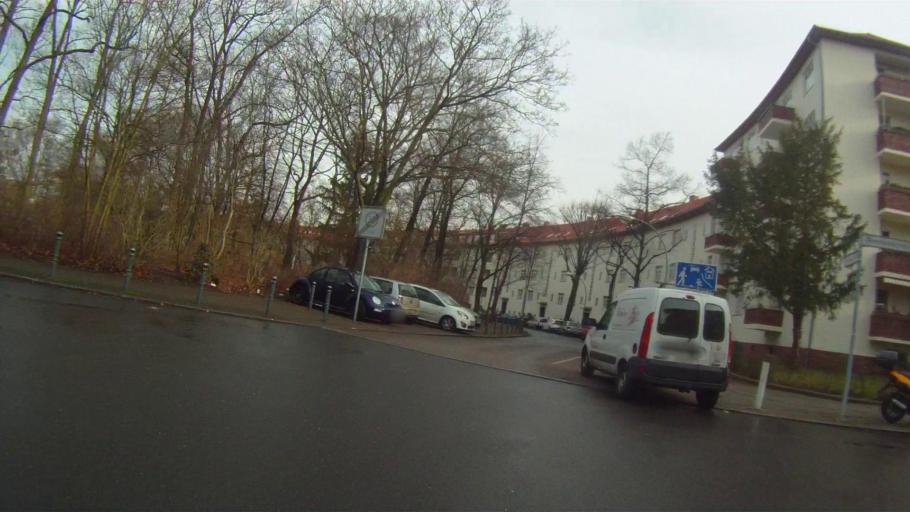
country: DE
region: Berlin
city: Schoneberg Bezirk
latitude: 52.4583
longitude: 13.3702
